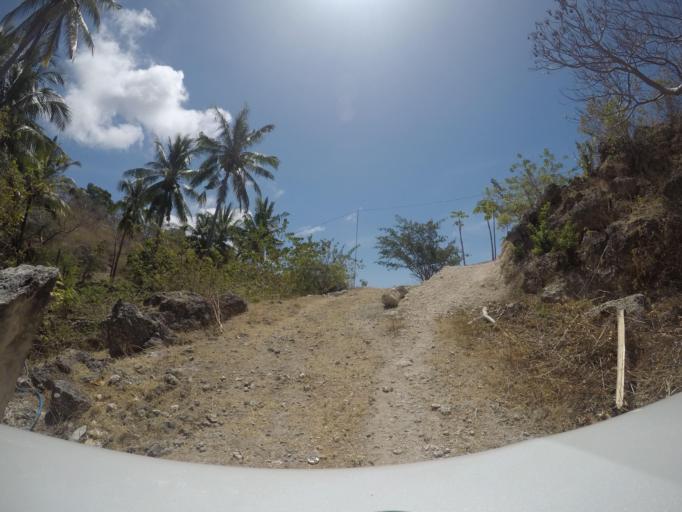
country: TL
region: Baucau
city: Baucau
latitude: -8.4438
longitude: 126.4414
